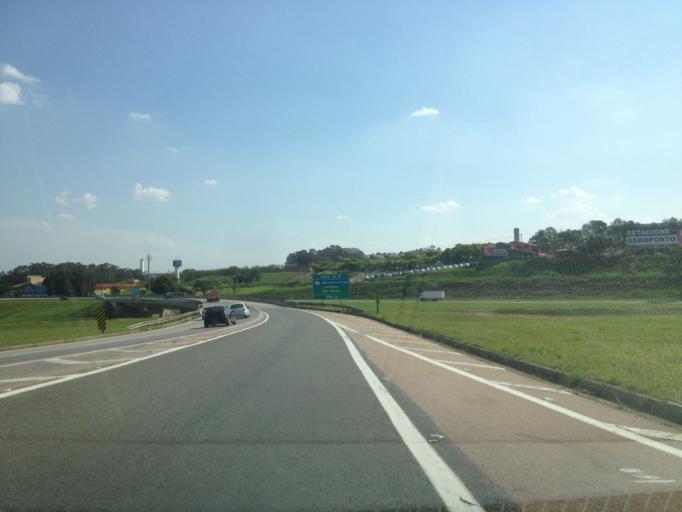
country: BR
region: Sao Paulo
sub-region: Campinas
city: Campinas
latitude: -22.9907
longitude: -47.1095
